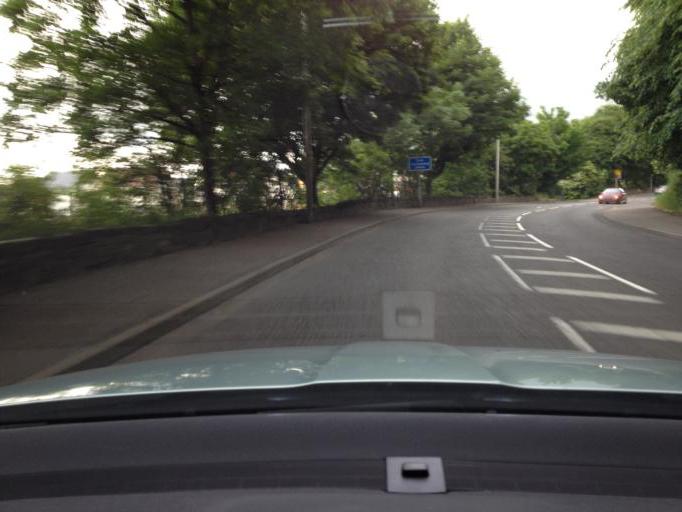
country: GB
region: Scotland
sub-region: Perth and Kinross
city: Perth
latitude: 56.3741
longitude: -3.4255
